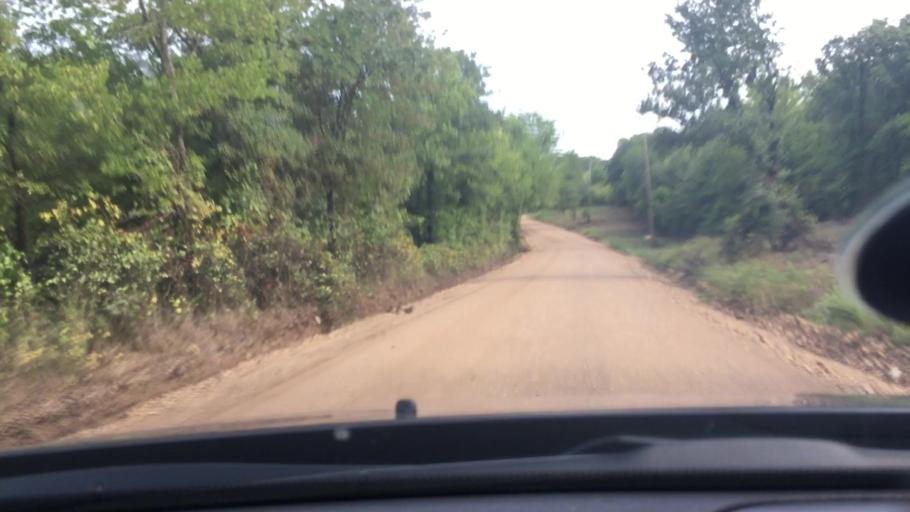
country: US
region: Oklahoma
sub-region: Atoka County
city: Atoka
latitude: 34.4446
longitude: -96.0672
